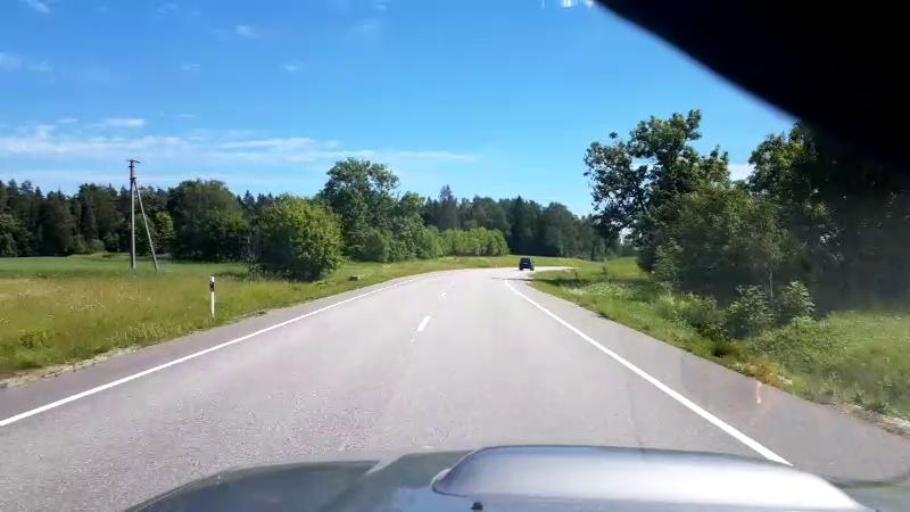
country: EE
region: Jaervamaa
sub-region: Jaerva-Jaani vald
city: Jarva-Jaani
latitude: 59.0138
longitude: 25.9173
